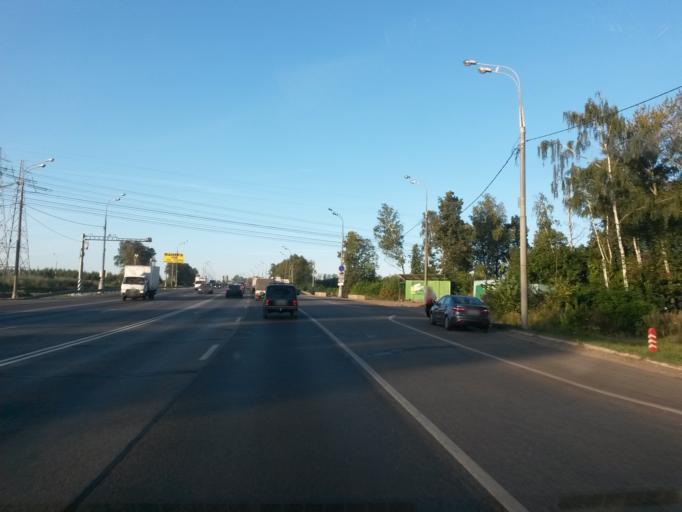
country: RU
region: Moskovskaya
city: Mamontovka
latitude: 55.9570
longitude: 37.8208
